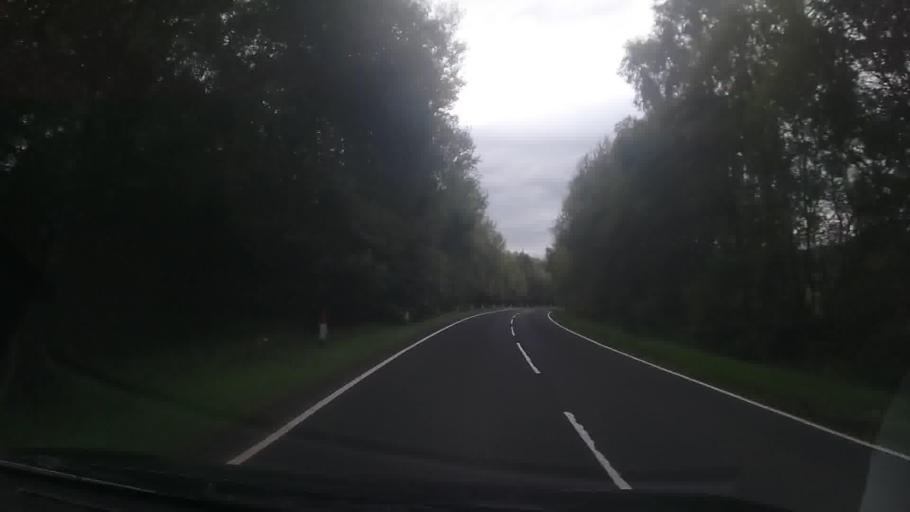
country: GB
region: Scotland
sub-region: Argyll and Bute
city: Garelochhead
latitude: 56.2260
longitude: -4.9854
